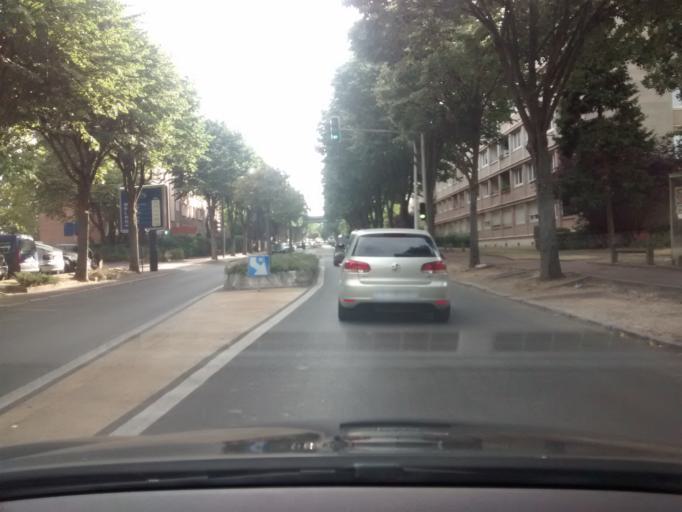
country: FR
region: Ile-de-France
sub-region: Departement des Hauts-de-Seine
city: Fontenay-aux-Roses
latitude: 48.7848
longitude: 2.2980
